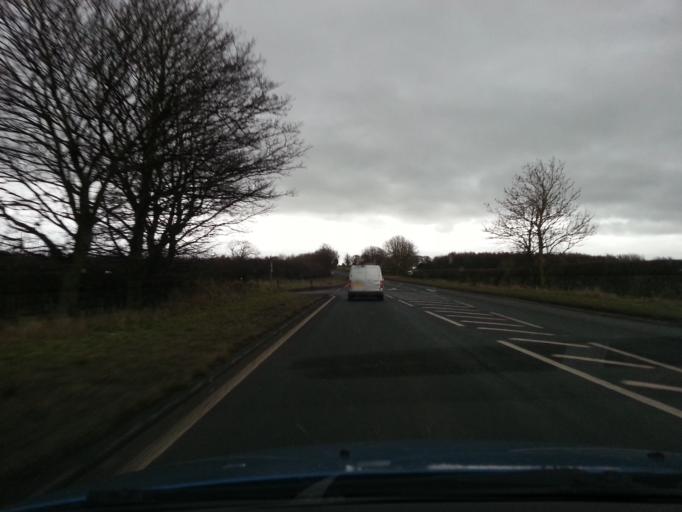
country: GB
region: England
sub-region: County Durham
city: Bishop Middleham
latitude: 54.6495
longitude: -1.4818
